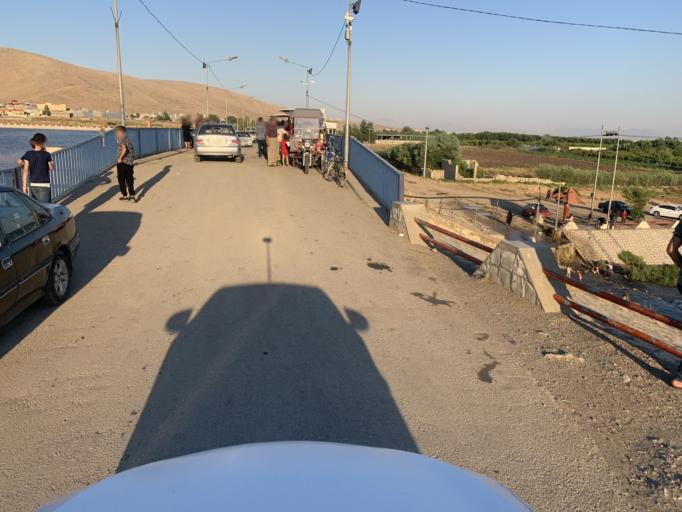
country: IQ
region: As Sulaymaniyah
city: Raniye
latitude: 36.2726
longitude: 44.7516
